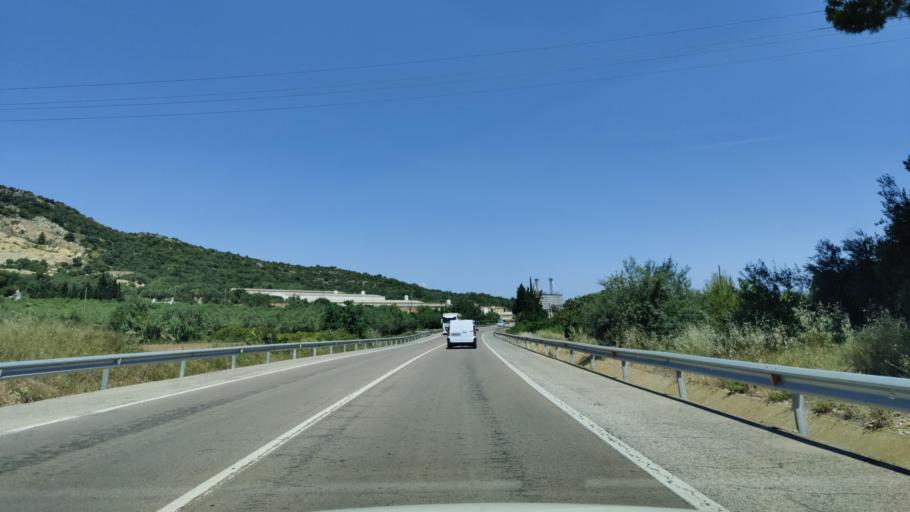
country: ES
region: Catalonia
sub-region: Provincia de Tarragona
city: Sant Carles de la Rapita
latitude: 40.6620
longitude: 0.5839
